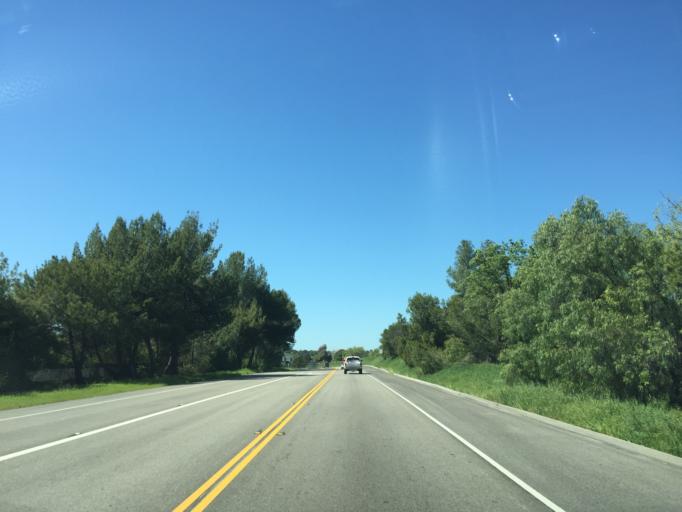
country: US
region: California
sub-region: Santa Barbara County
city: Los Olivos
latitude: 34.6659
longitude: -120.1106
